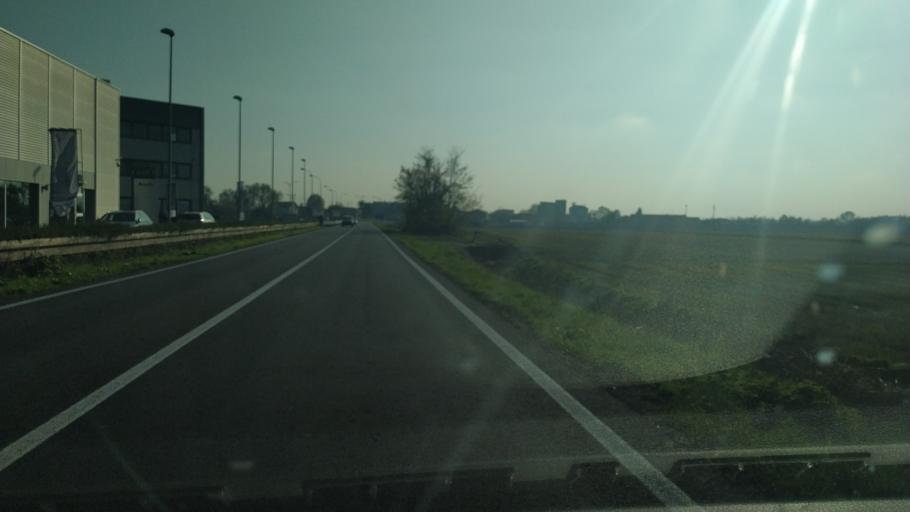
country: IT
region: Piedmont
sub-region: Provincia di Vercelli
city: Borgo Vercelli
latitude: 45.3437
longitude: 8.4520
